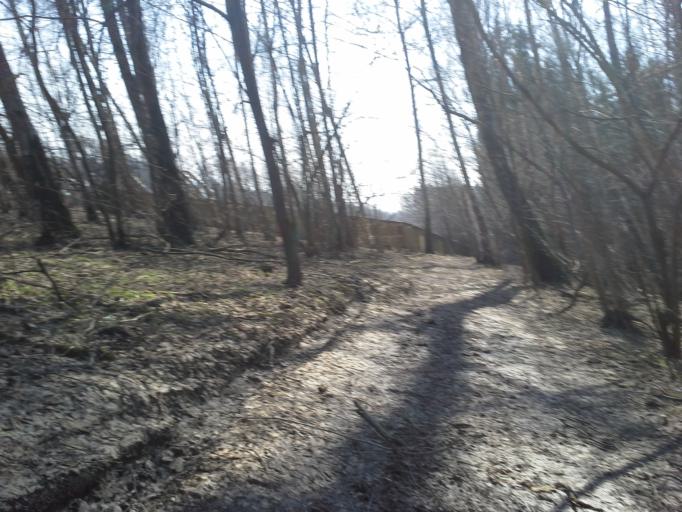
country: RU
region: Moskovskaya
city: Filimonki
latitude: 55.5469
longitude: 37.3861
